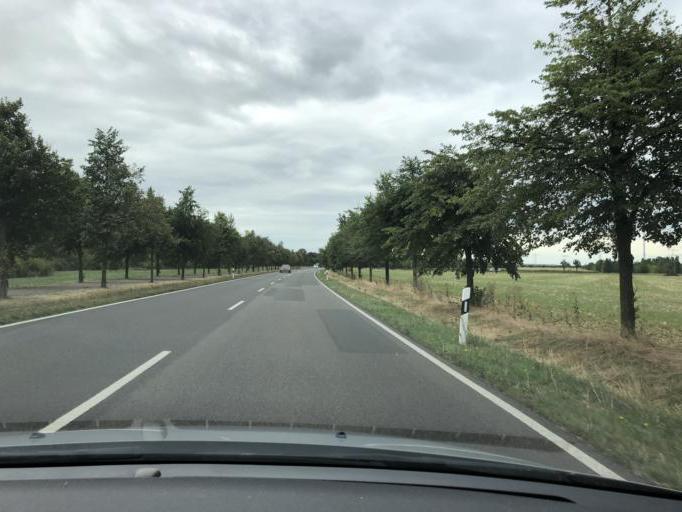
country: DE
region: Saxony
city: Rackwitz
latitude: 51.4151
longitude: 12.4160
